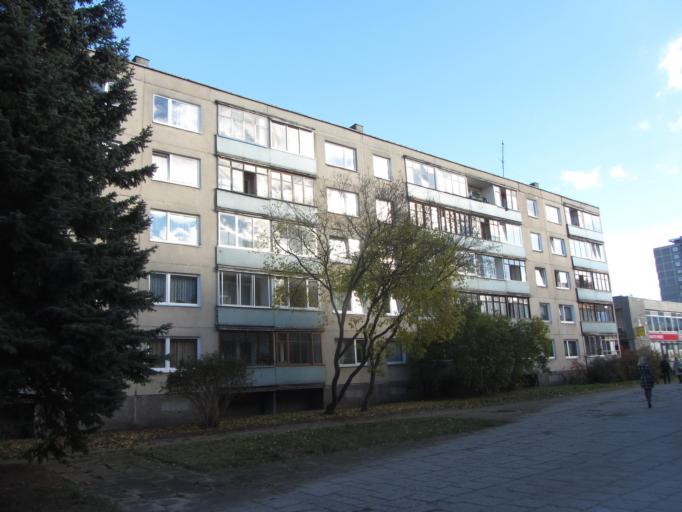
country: LT
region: Vilnius County
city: Lazdynai
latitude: 54.6766
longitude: 25.2134
